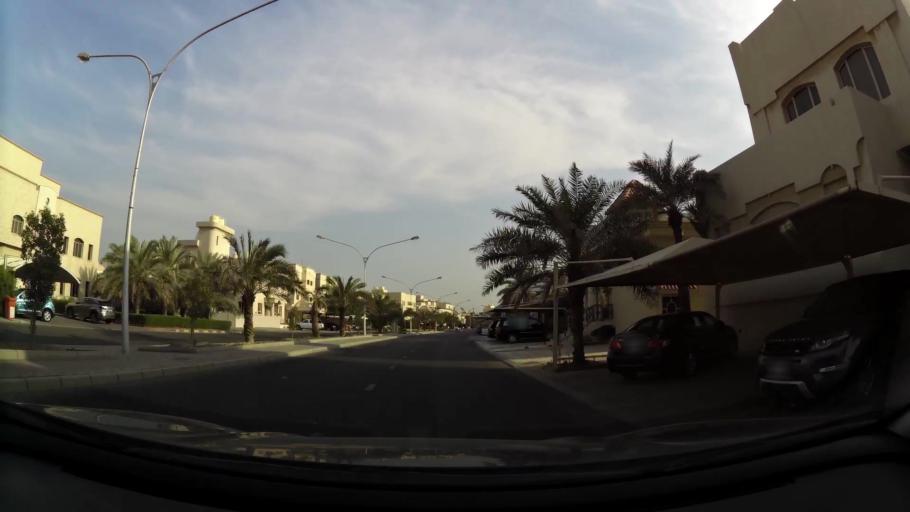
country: KW
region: Muhafazat Hawalli
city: Hawalli
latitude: 29.3112
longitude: 48.0136
